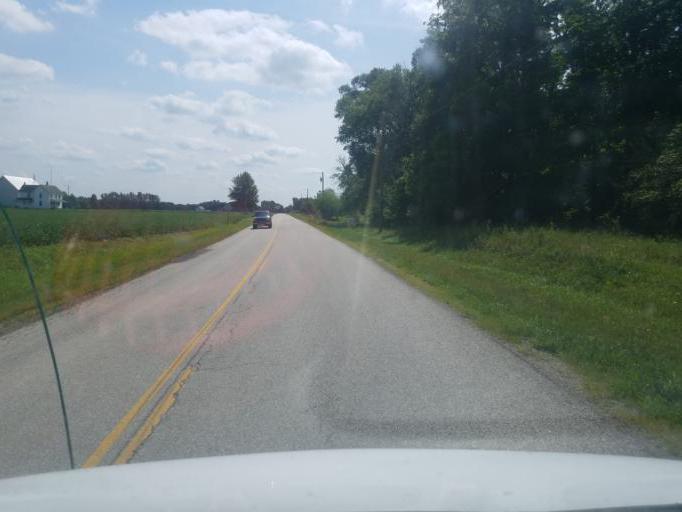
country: US
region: Ohio
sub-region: Union County
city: Richwood
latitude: 40.3215
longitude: -83.2982
